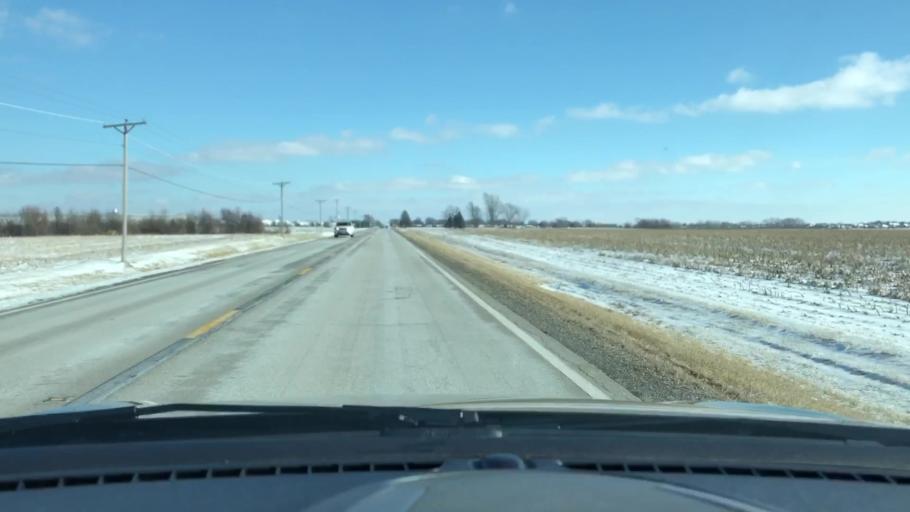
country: US
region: Illinois
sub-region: Will County
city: Ingalls Park
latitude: 41.4822
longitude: -88.0170
